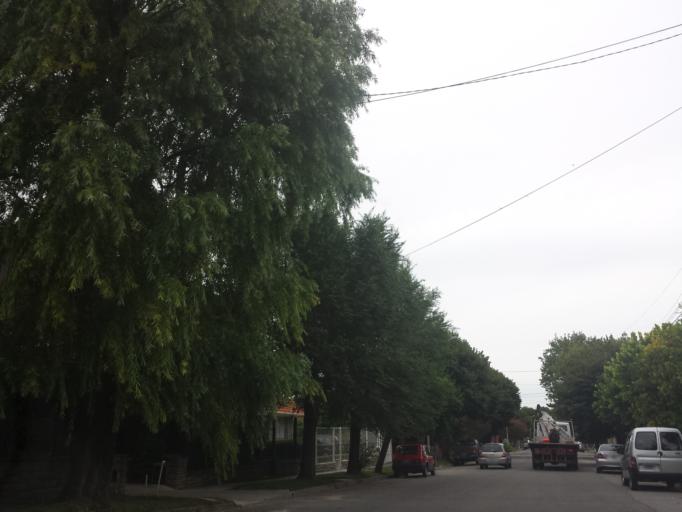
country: AR
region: Buenos Aires
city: Mar del Plata
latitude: -38.0186
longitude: -57.5384
